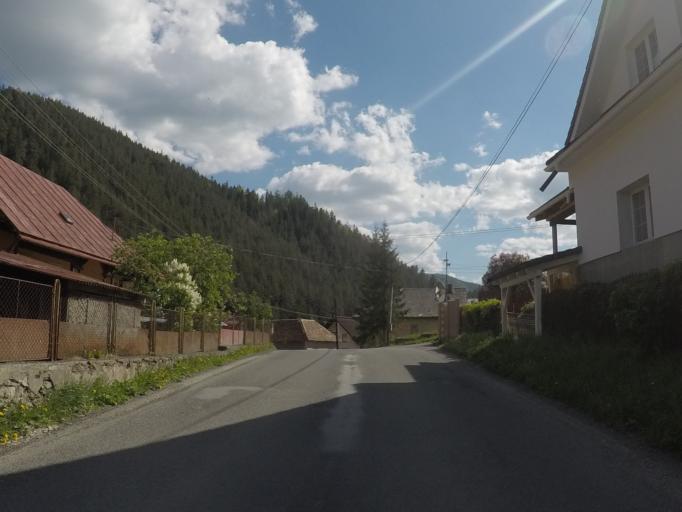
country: SK
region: Kosicky
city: Dobsina
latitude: 48.9202
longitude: 20.2725
